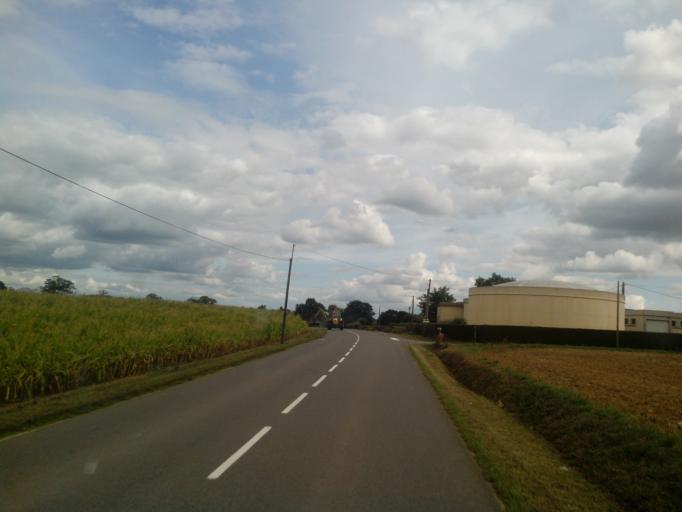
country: FR
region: Brittany
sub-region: Departement d'Ille-et-Vilaine
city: Melesse
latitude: 48.1973
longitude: -1.7091
